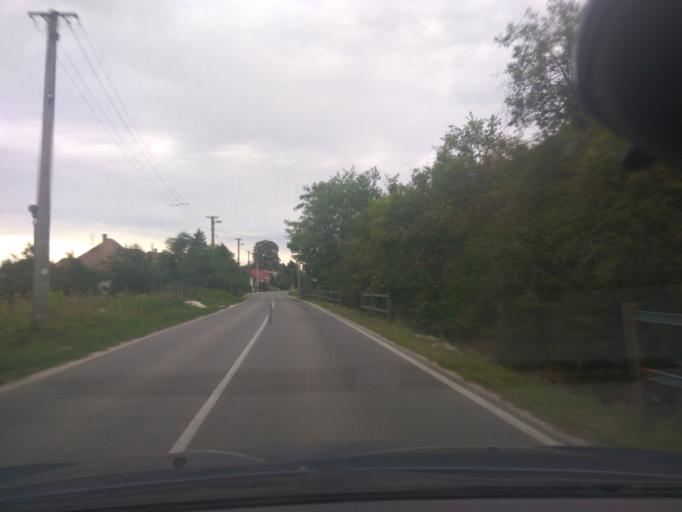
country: SK
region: Trnavsky
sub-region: Okres Trnava
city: Piestany
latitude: 48.6260
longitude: 17.8696
